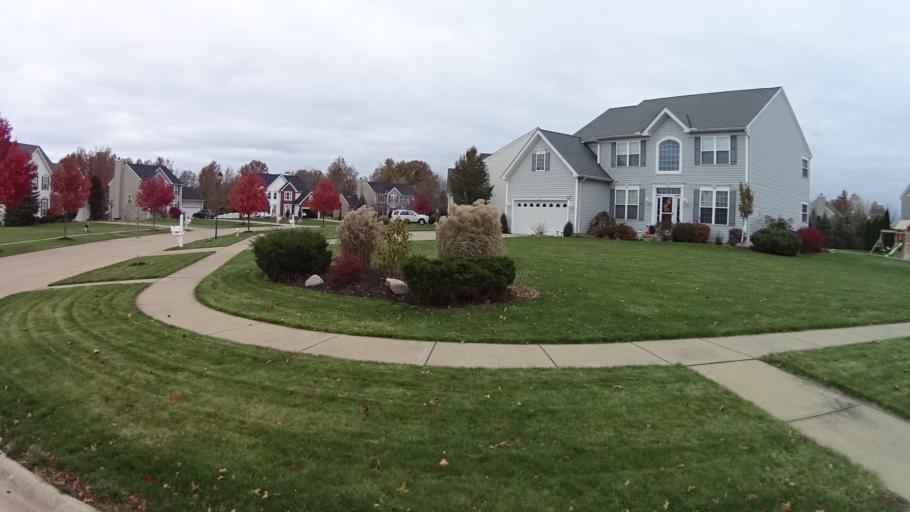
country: US
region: Ohio
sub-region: Lorain County
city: Avon Lake
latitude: 41.4918
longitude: -82.0425
